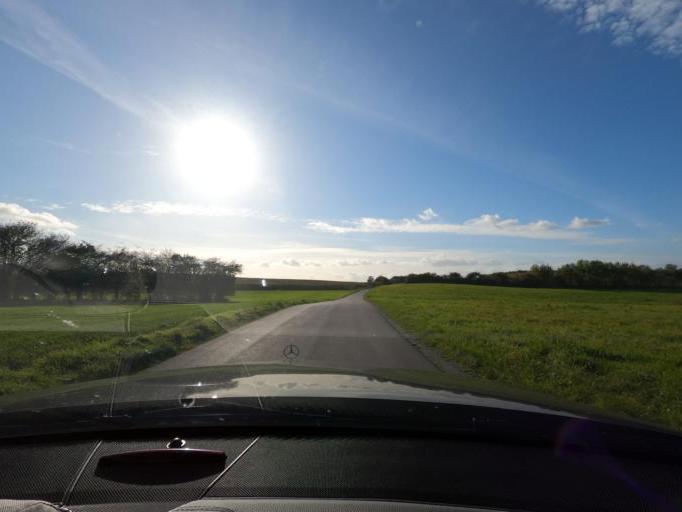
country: DK
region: South Denmark
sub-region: Sonderborg Kommune
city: Broager
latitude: 54.8815
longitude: 9.7107
